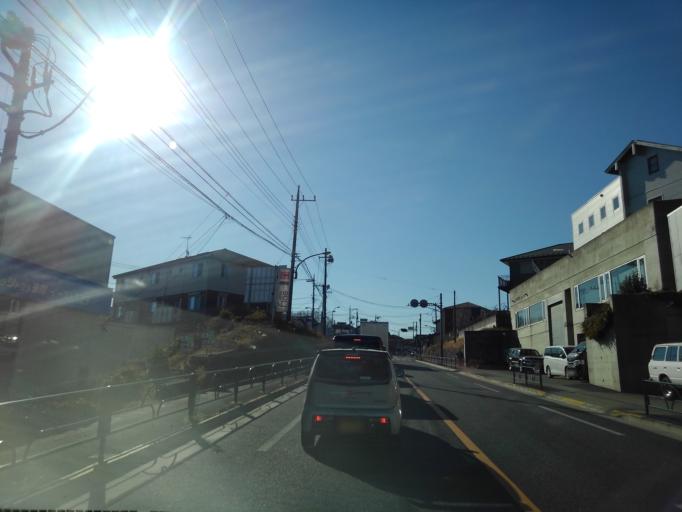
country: JP
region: Tokyo
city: Hino
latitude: 35.6865
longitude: 139.3706
